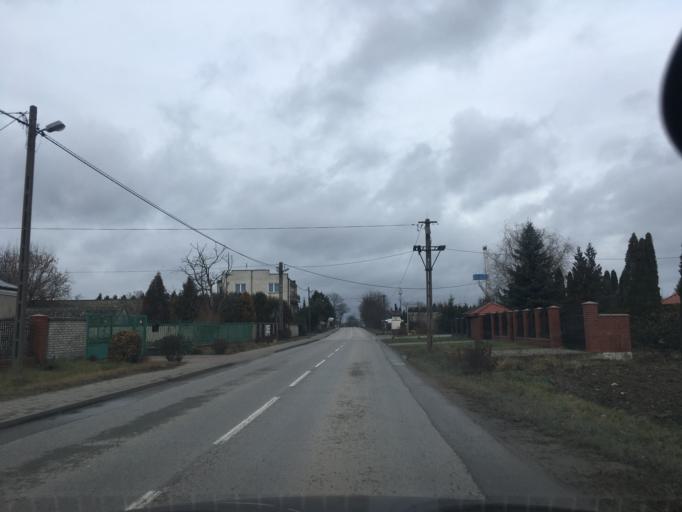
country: PL
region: Masovian Voivodeship
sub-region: Powiat piaseczynski
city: Lesznowola
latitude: 52.1113
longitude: 20.9314
